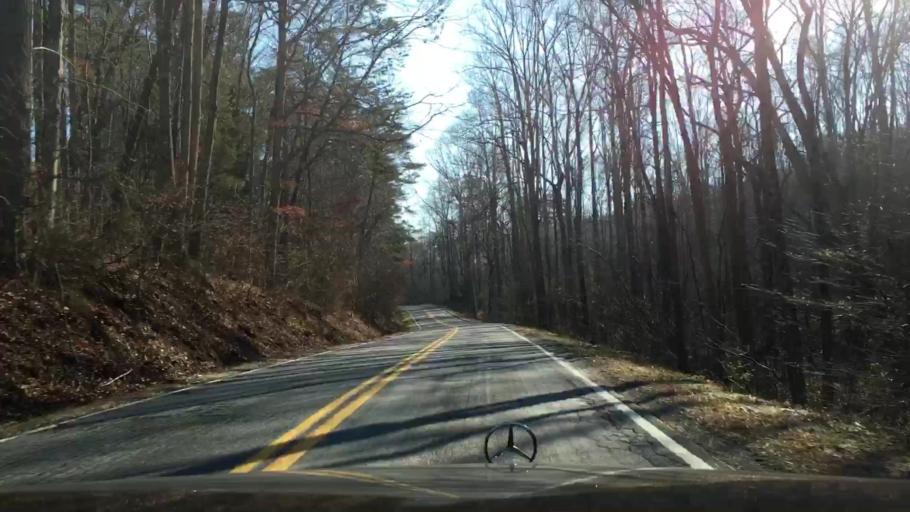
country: US
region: Virginia
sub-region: Campbell County
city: Altavista
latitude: 37.1438
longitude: -79.3291
